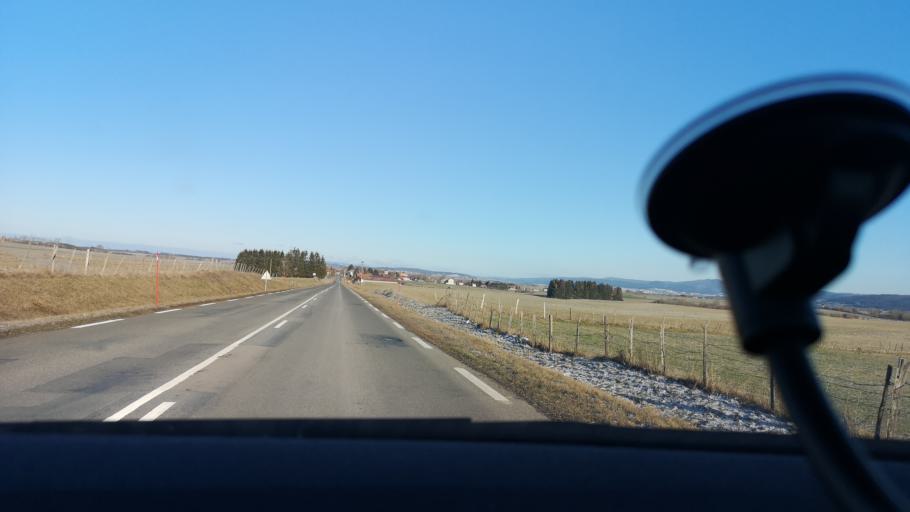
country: FR
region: Franche-Comte
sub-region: Departement du Doubs
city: Frasne
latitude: 46.8621
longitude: 6.1698
